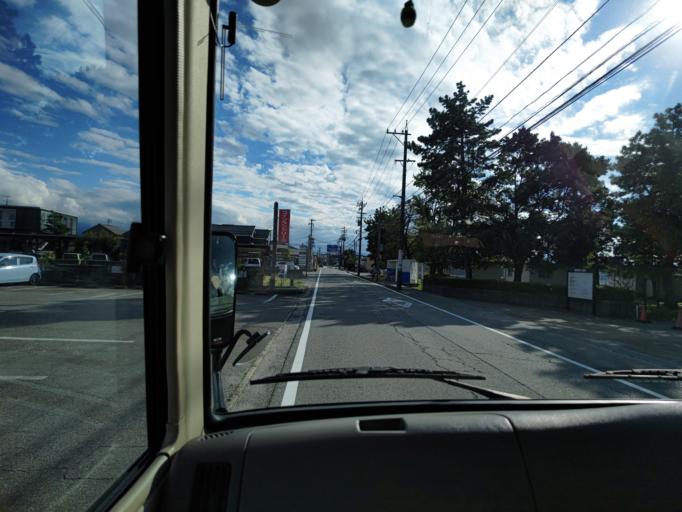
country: JP
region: Toyama
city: Nyuzen
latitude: 36.8826
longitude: 137.4467
